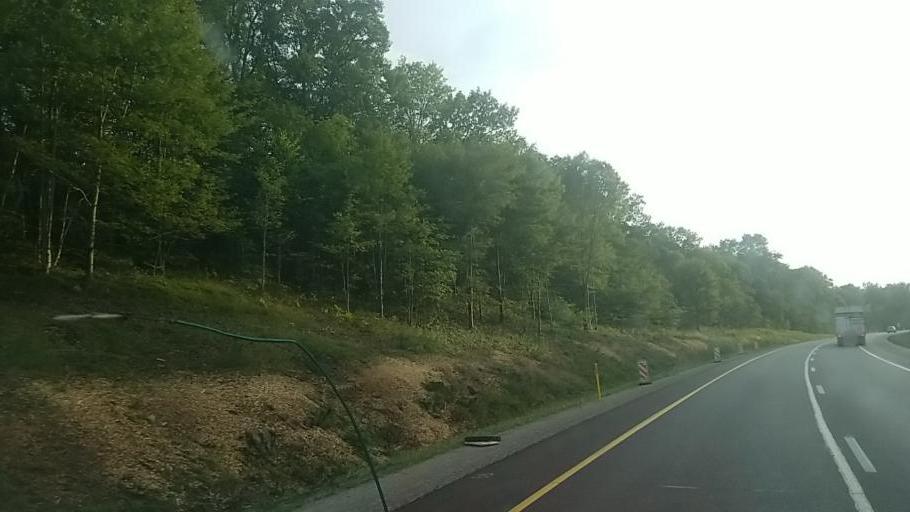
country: US
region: Pennsylvania
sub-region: Clearfield County
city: Troy
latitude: 40.9762
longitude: -78.0450
